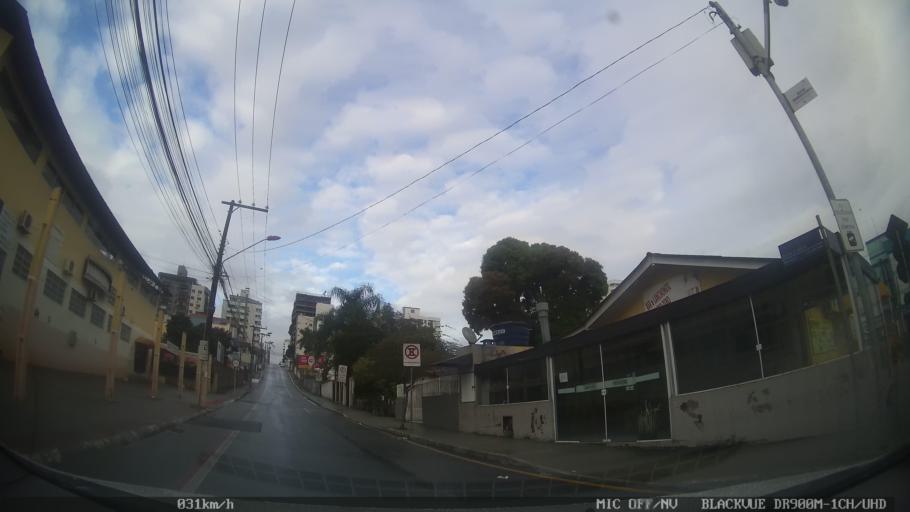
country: BR
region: Santa Catarina
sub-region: Sao Jose
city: Campinas
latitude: -27.5739
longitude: -48.6049
